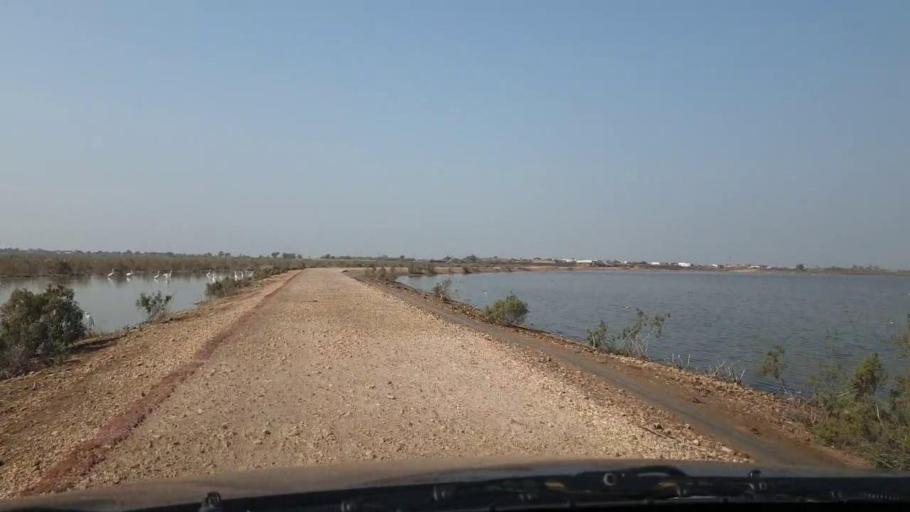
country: PK
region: Sindh
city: Jhol
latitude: 25.9023
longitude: 69.0037
